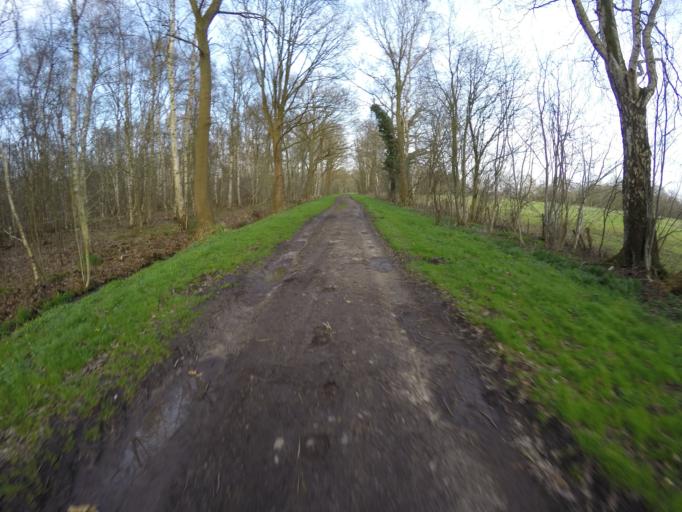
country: DE
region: Schleswig-Holstein
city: Hemdingen
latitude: 53.7278
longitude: 9.8454
